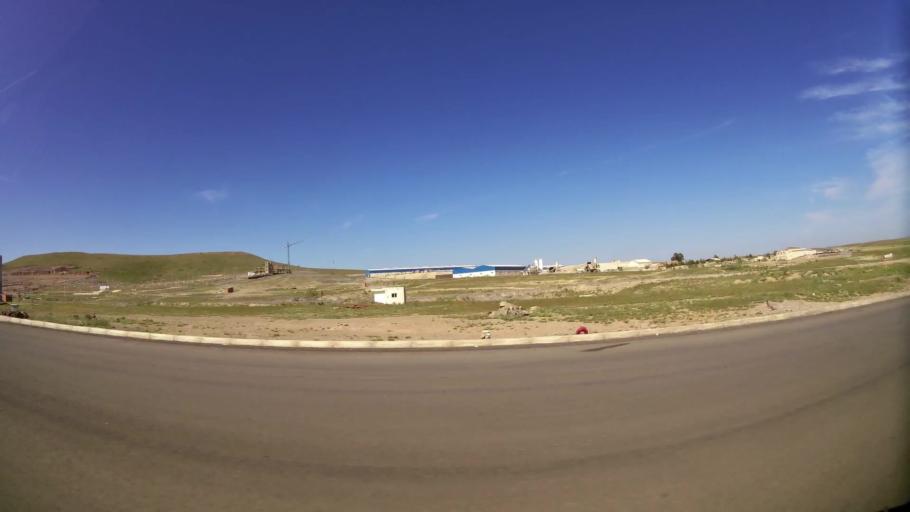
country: MA
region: Oriental
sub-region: Oujda-Angad
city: Oujda
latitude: 34.6523
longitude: -1.9552
